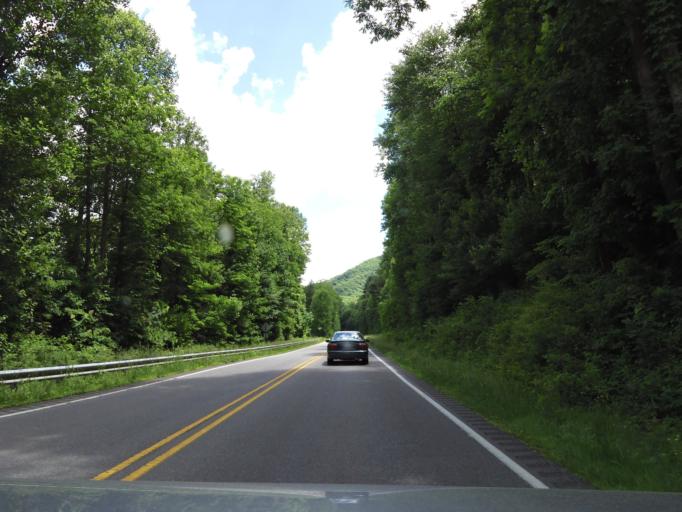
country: US
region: North Carolina
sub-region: Graham County
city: Robbinsville
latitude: 35.2716
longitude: -83.7238
